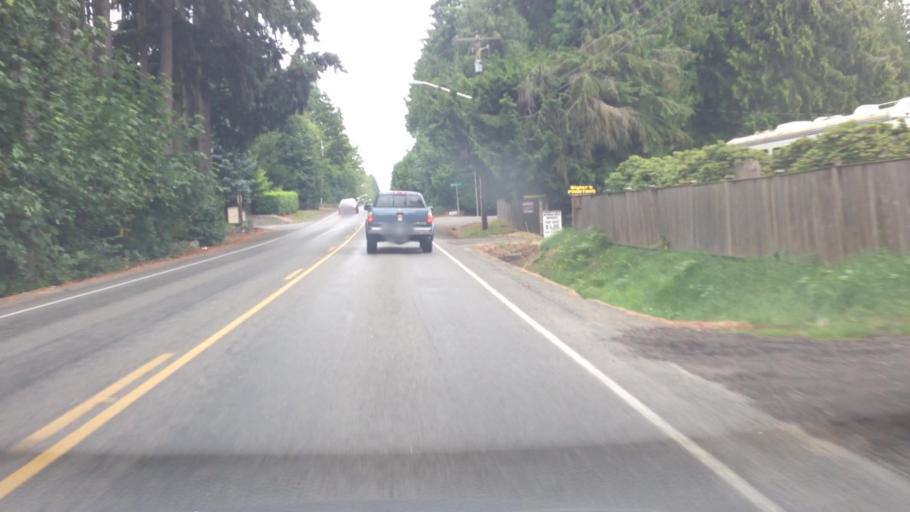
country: US
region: Washington
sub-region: Pierce County
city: South Hill
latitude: 47.1184
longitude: -122.2979
